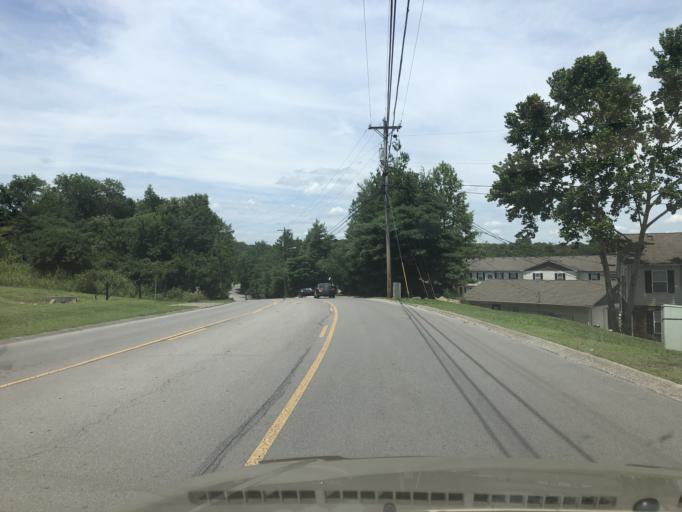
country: US
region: Tennessee
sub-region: Davidson County
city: Lakewood
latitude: 36.2559
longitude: -86.6739
